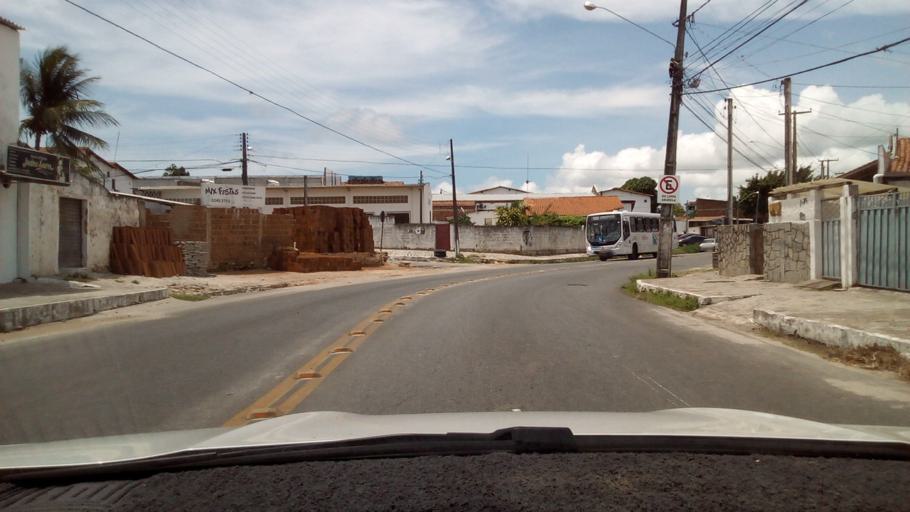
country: BR
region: Paraiba
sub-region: Joao Pessoa
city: Joao Pessoa
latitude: -7.1767
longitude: -34.8444
